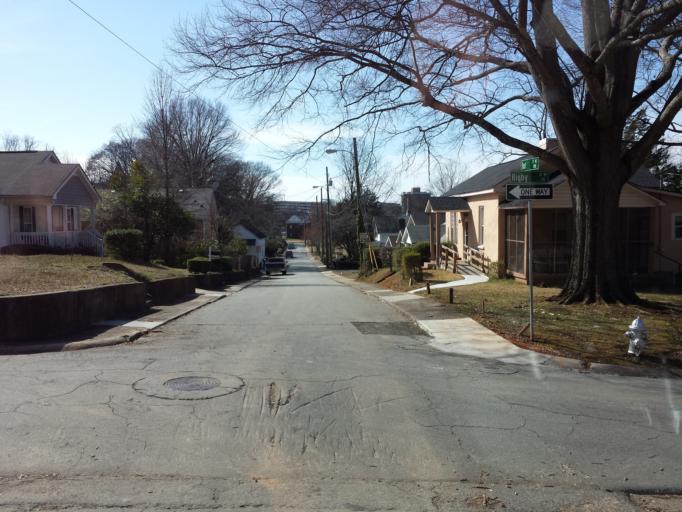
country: US
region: Georgia
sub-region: Cobb County
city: Marietta
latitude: 33.9540
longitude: -84.5406
